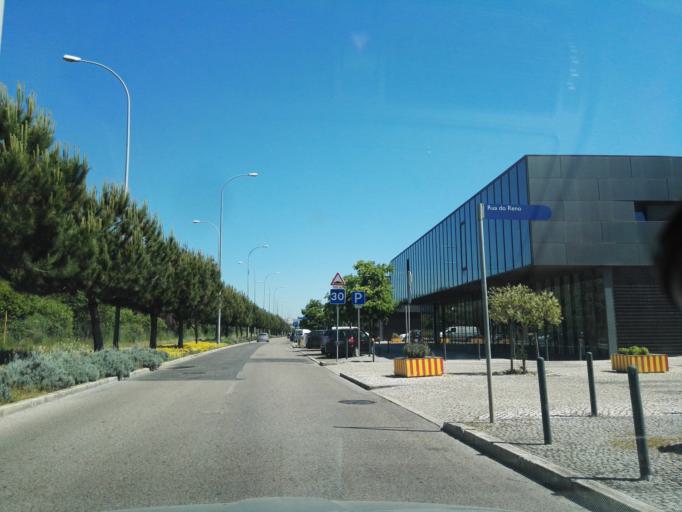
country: PT
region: Lisbon
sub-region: Loures
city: Sacavem
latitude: 38.7898
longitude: -9.0996
